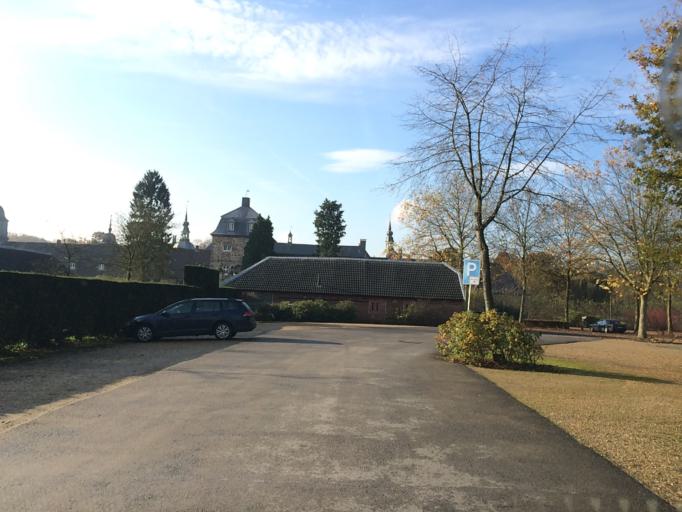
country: DE
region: North Rhine-Westphalia
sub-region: Regierungsbezirk Munster
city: Klein Reken
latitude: 51.7435
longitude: 7.0023
